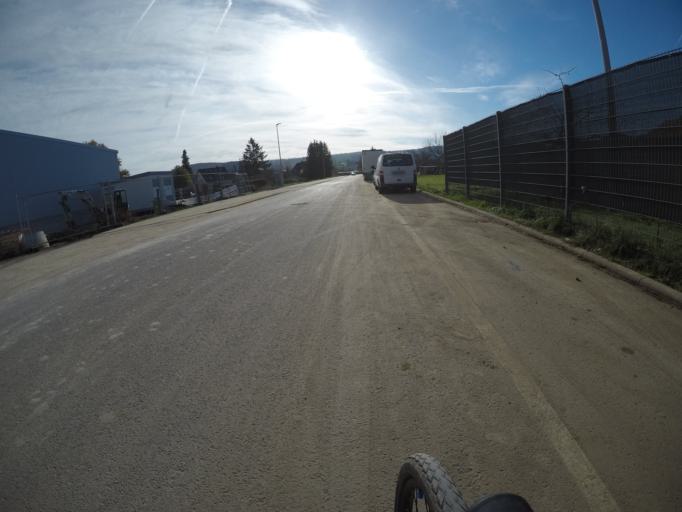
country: DE
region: Baden-Wuerttemberg
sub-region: Regierungsbezirk Stuttgart
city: Schorndorf
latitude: 48.8107
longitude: 9.5381
